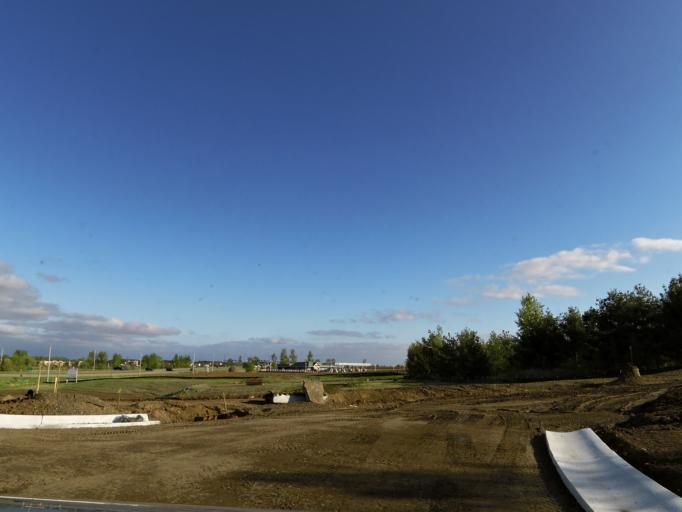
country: US
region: Minnesota
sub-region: Washington County
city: Lake Elmo
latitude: 44.9539
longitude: -92.9050
